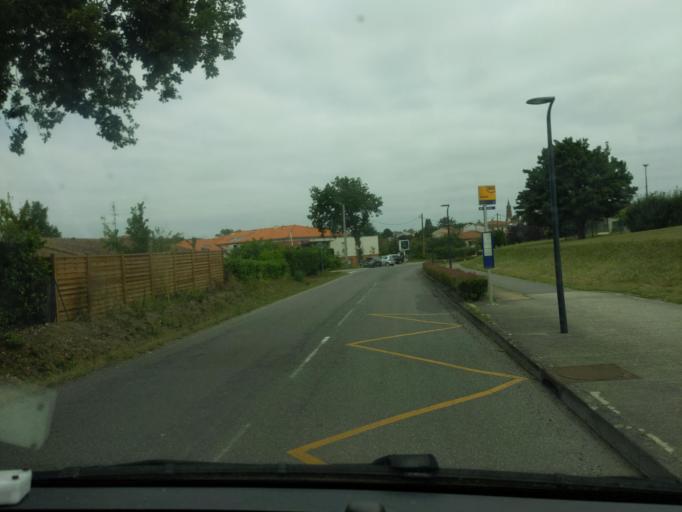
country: FR
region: Midi-Pyrenees
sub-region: Departement de la Haute-Garonne
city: Escalquens
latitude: 43.5189
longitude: 1.5536
